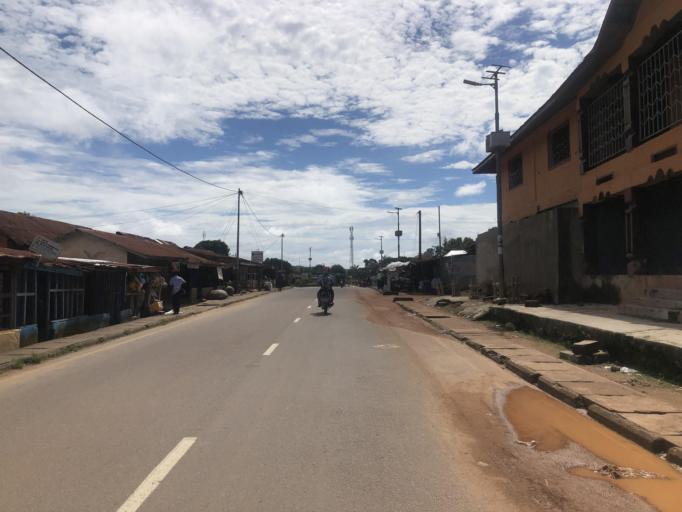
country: SL
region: Eastern Province
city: Koidu
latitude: 8.6386
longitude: -10.9725
